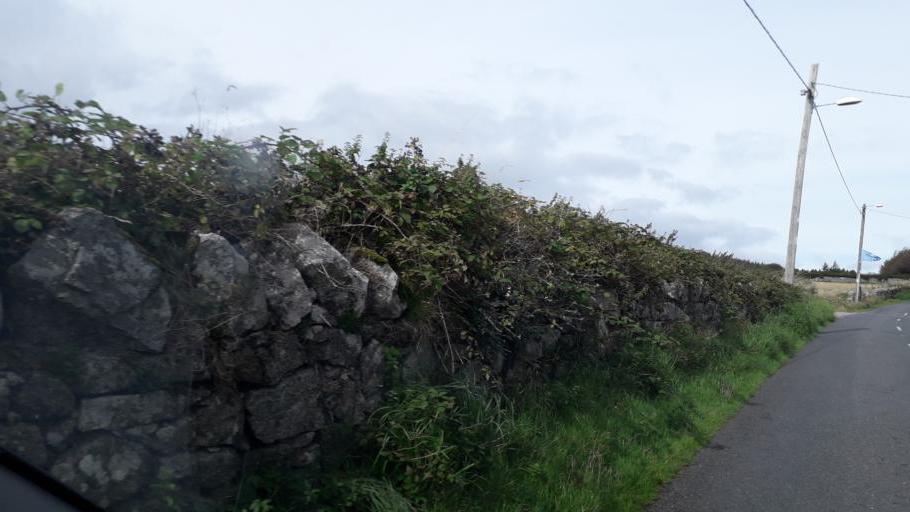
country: IE
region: Leinster
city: Sandyford
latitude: 53.2242
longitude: -6.2203
